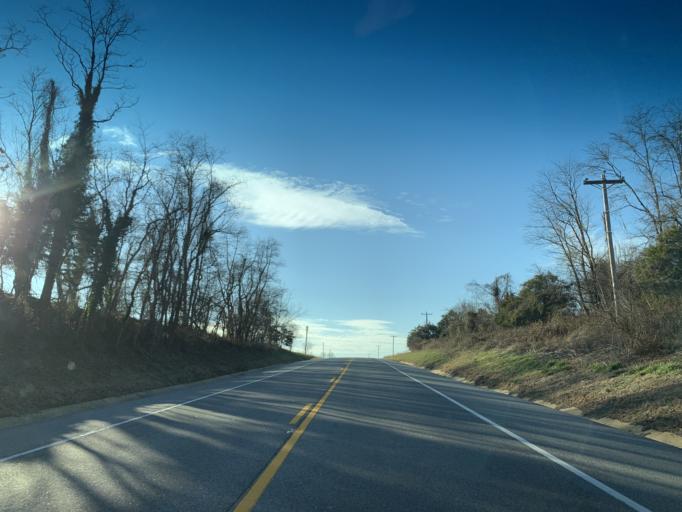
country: US
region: Delaware
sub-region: New Castle County
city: Middletown
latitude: 39.3399
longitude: -75.8904
